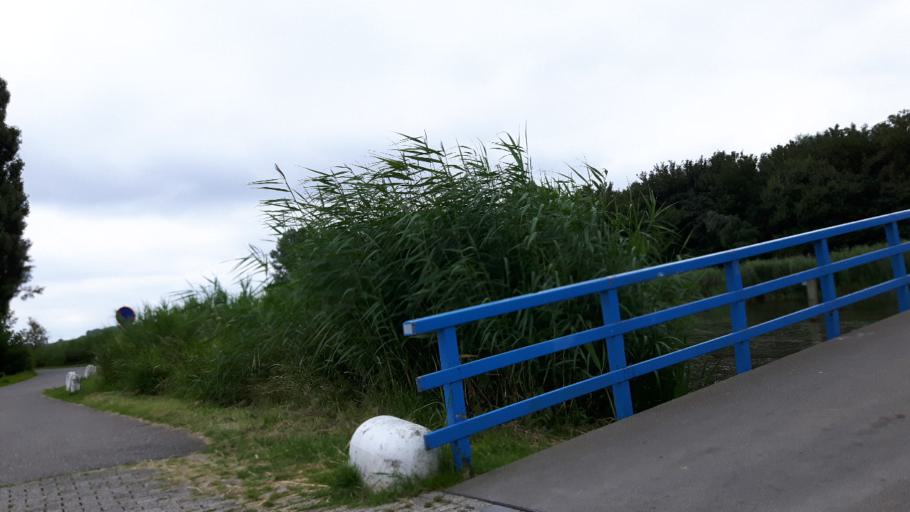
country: NL
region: South Holland
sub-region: Gemeente Lansingerland
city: Bleiswijk
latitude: 51.9909
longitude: 4.5471
